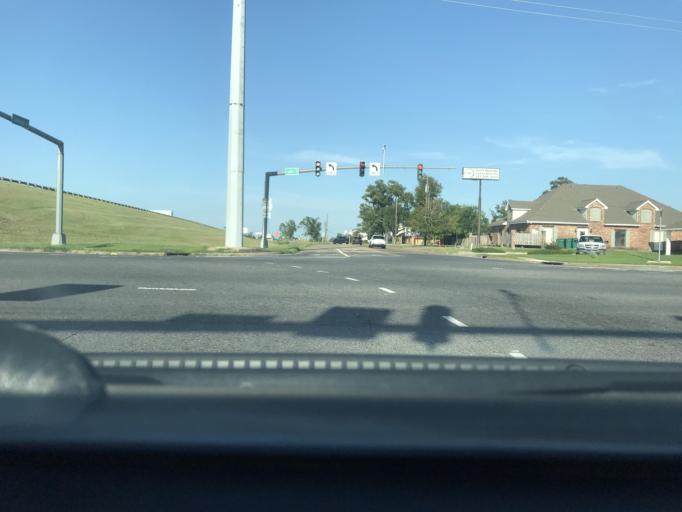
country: US
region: Louisiana
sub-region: Calcasieu Parish
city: Lake Charles
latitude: 30.1965
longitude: -93.2325
